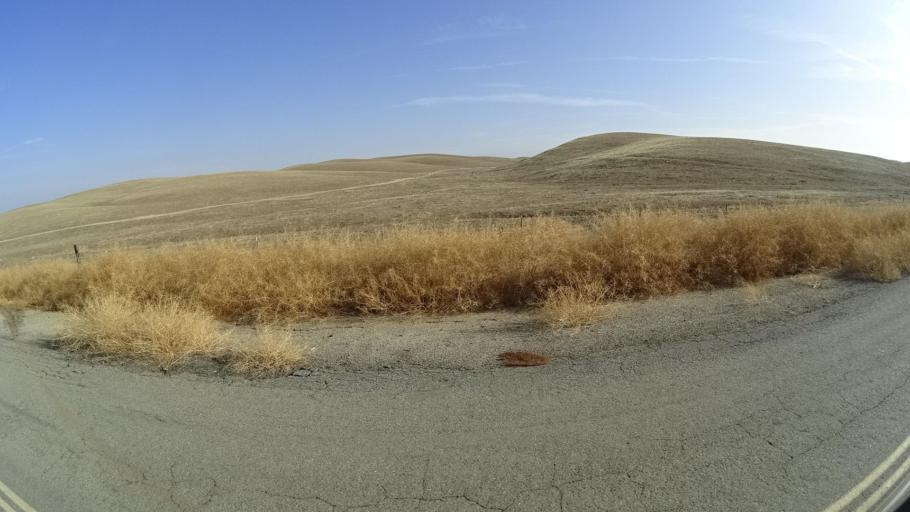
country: US
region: California
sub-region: Tulare County
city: Richgrove
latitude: 35.6352
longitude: -119.0362
